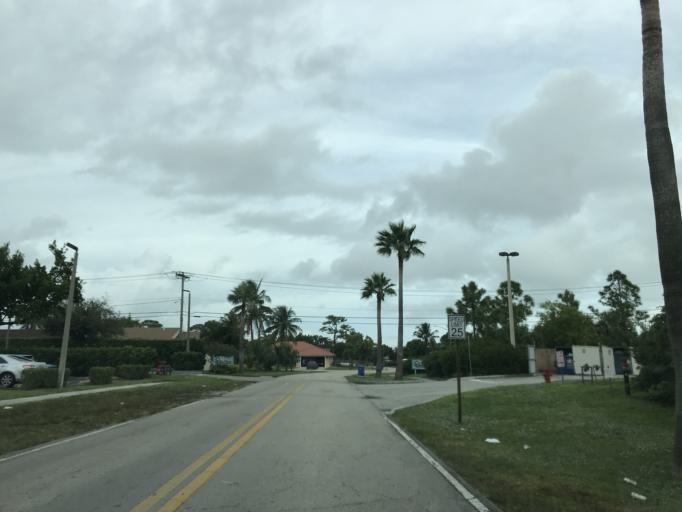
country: US
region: Florida
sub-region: Palm Beach County
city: Hypoluxo
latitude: 26.5726
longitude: -80.0626
